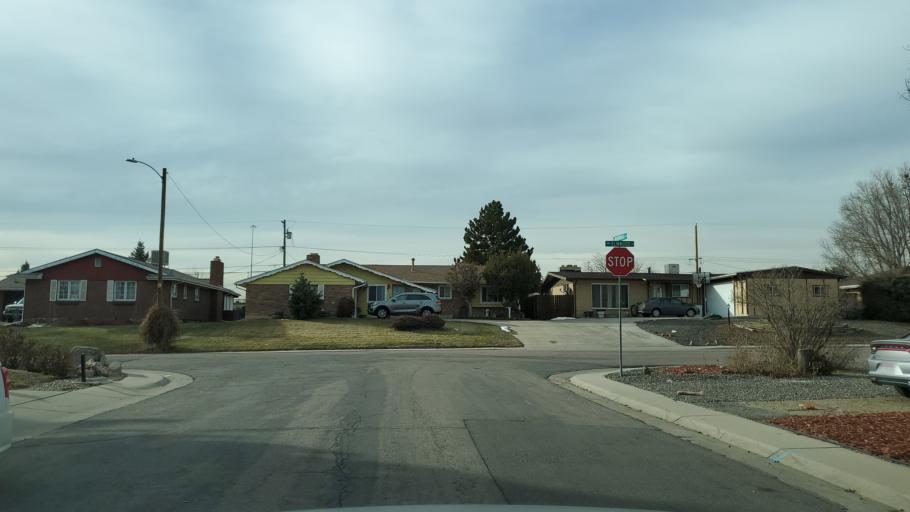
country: US
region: Colorado
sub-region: Adams County
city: Westminster
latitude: 39.8369
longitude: -105.0206
